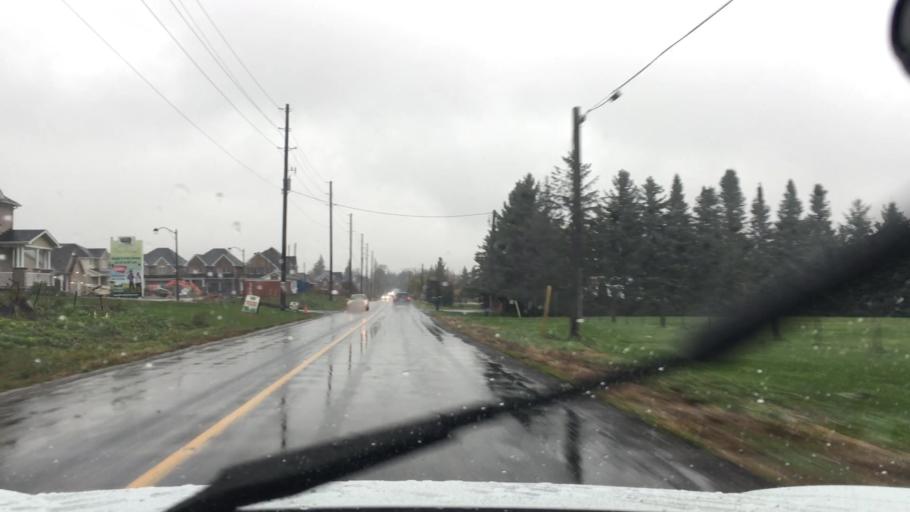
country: CA
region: Ontario
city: Oshawa
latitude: 43.9555
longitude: -78.8349
